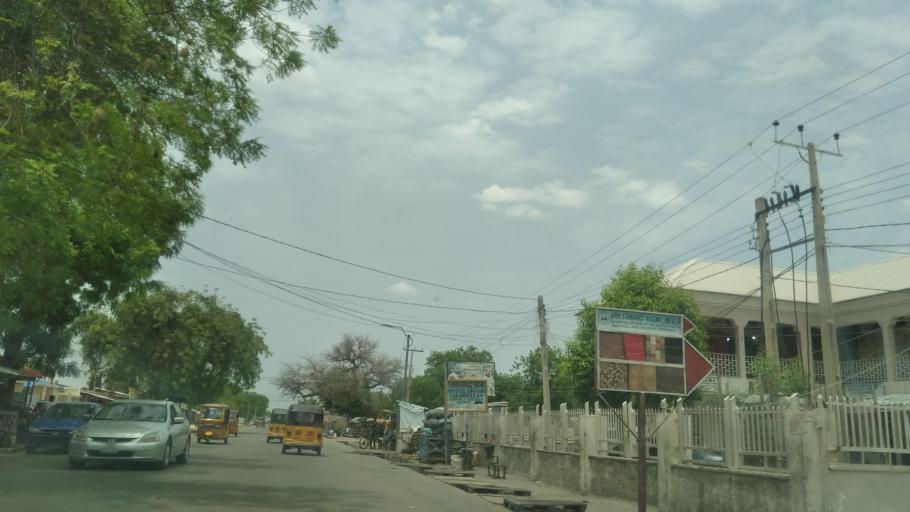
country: NG
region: Borno
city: Maiduguri
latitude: 11.8061
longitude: 13.1626
